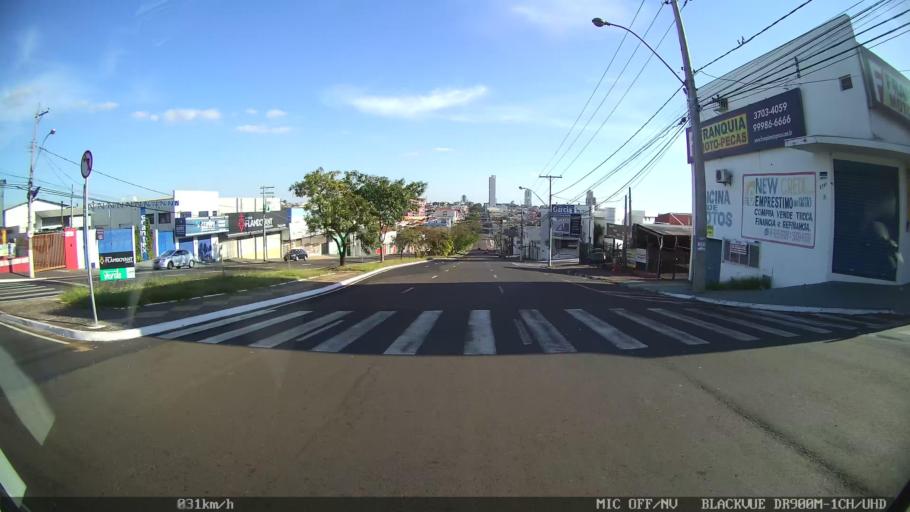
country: BR
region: Sao Paulo
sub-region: Franca
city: Franca
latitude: -20.5183
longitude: -47.3824
